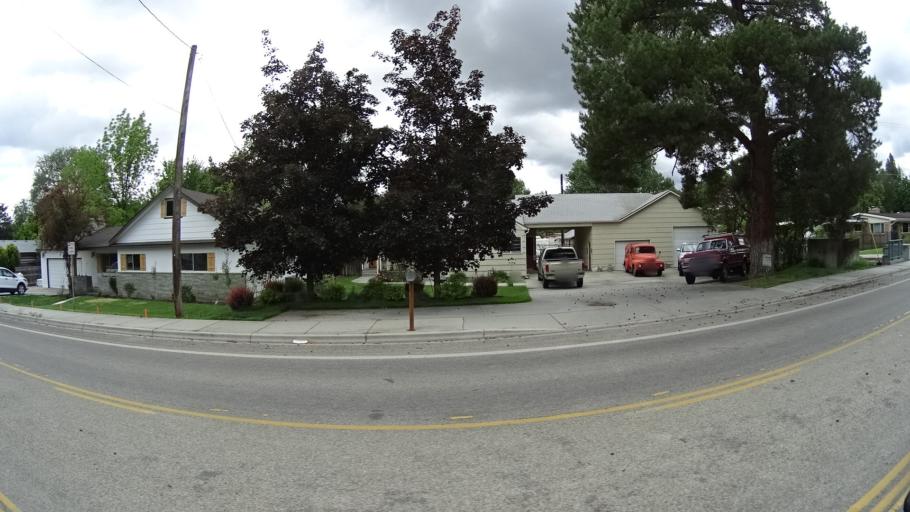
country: US
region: Idaho
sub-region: Ada County
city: Garden City
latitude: 43.6512
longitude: -116.2333
